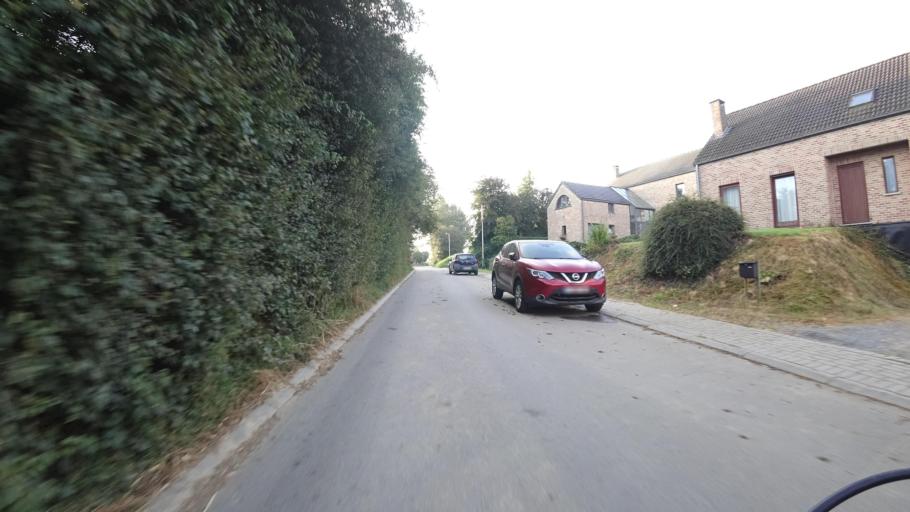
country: BE
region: Wallonia
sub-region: Province du Brabant Wallon
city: Walhain-Saint-Paul
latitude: 50.6195
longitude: 4.6982
